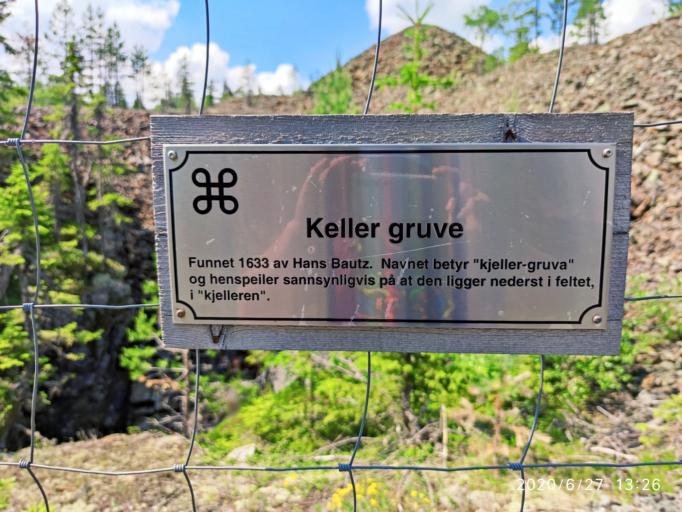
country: NO
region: Buskerud
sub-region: Kongsberg
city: Kongsberg
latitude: 59.6609
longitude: 9.5886
